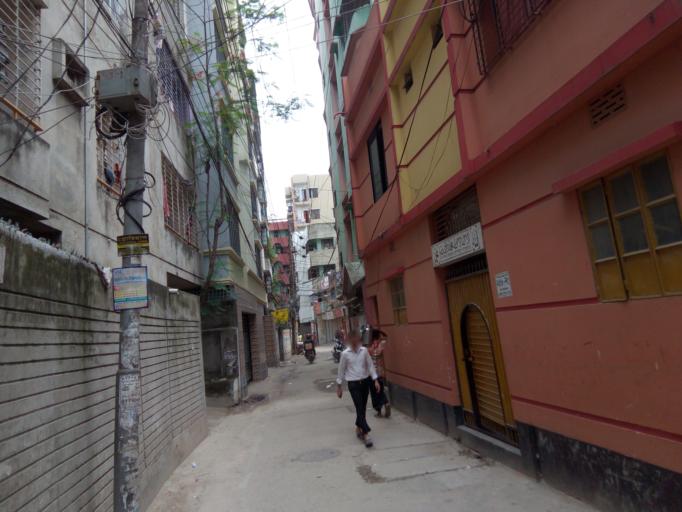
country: BD
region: Dhaka
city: Azimpur
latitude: 23.7498
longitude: 90.3643
